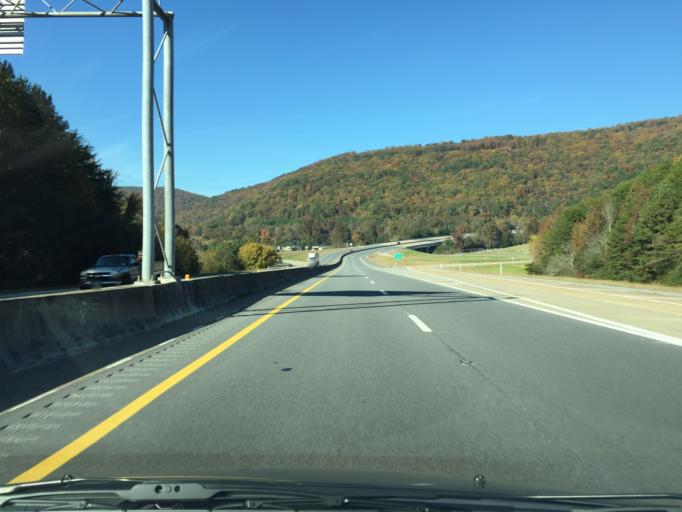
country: US
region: Tennessee
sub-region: Hamilton County
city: Soddy-Daisy
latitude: 35.3038
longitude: -85.1570
